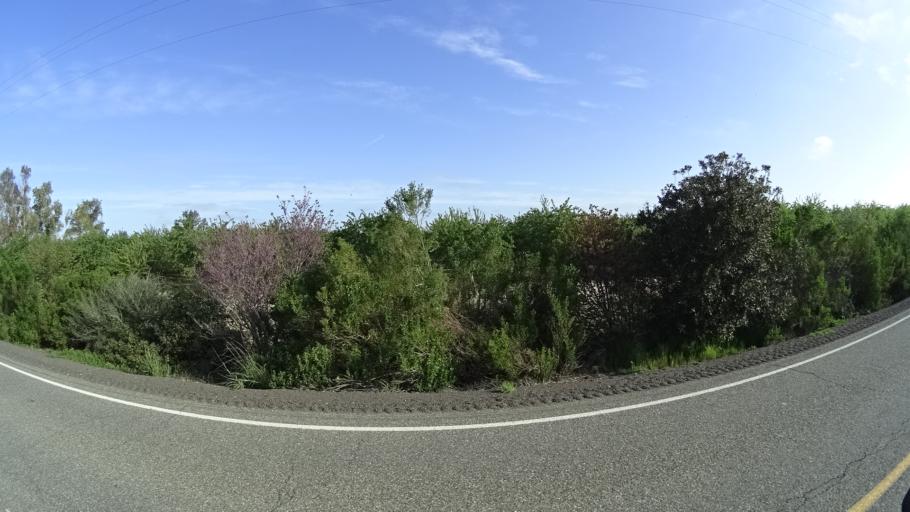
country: US
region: California
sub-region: Glenn County
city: Willows
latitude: 39.5822
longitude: -122.1546
